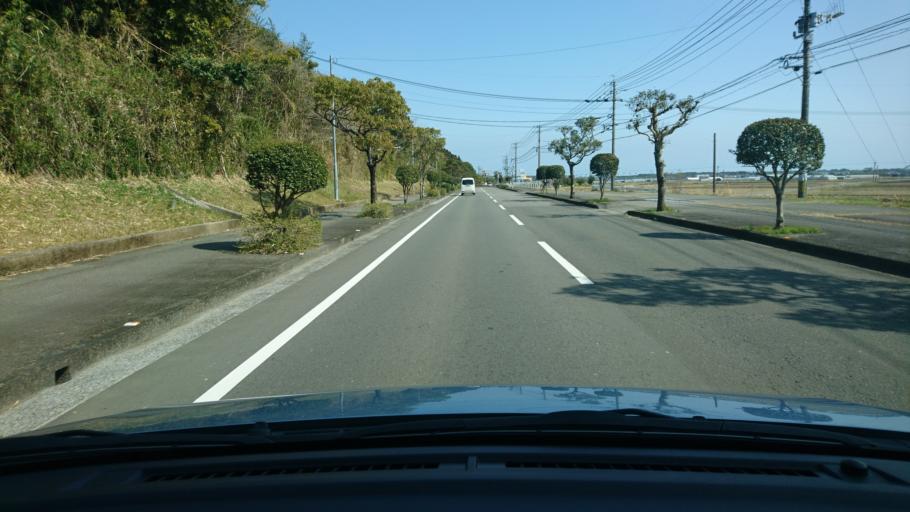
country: JP
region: Miyazaki
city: Miyazaki-shi
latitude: 31.8257
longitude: 131.4279
